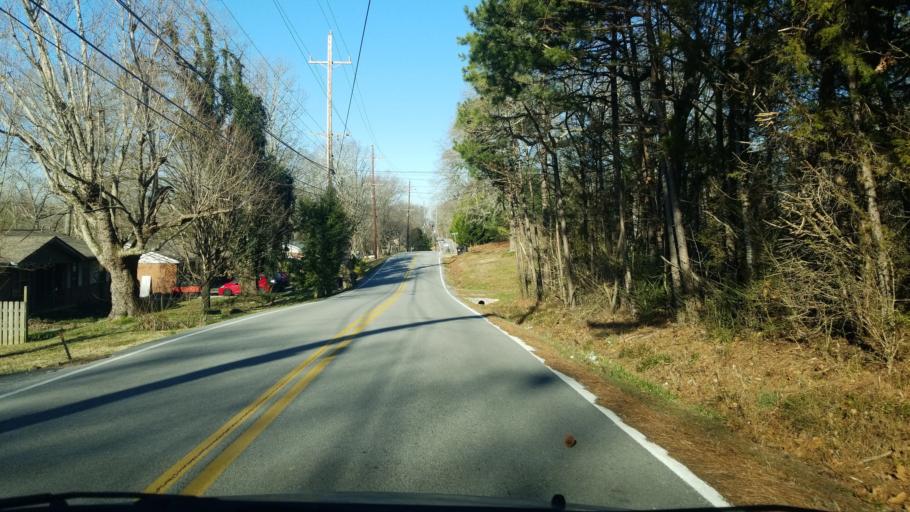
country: US
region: Tennessee
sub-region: Hamilton County
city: Collegedale
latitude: 35.0393
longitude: -85.0937
